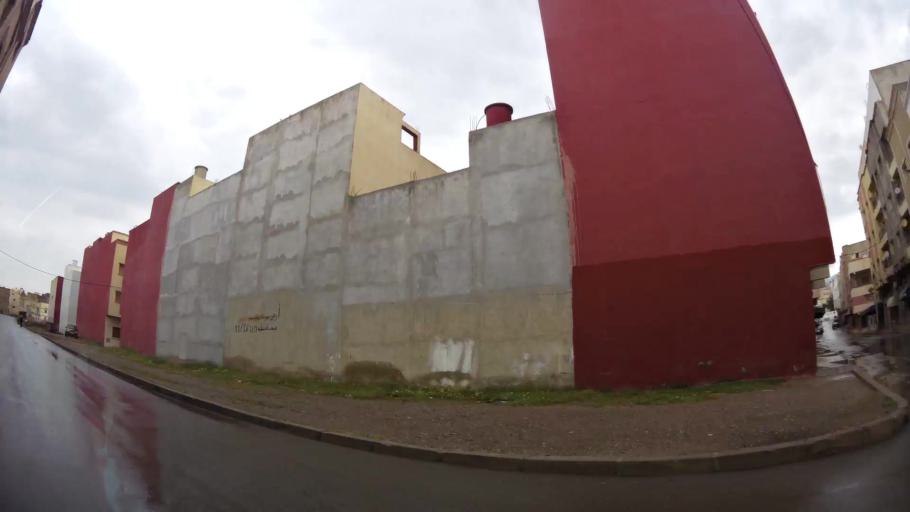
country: MA
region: Oriental
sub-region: Nador
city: Nador
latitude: 35.1533
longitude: -2.9992
